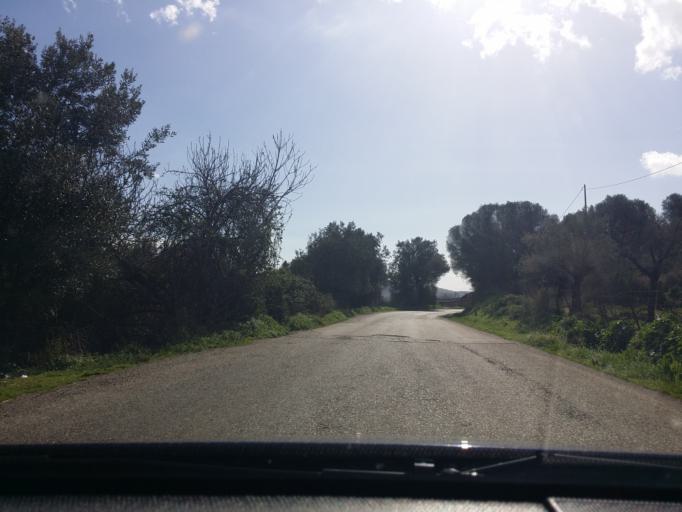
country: GR
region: West Greece
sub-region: Nomos Aitolias kai Akarnanias
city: Astakos
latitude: 38.5583
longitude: 21.0974
